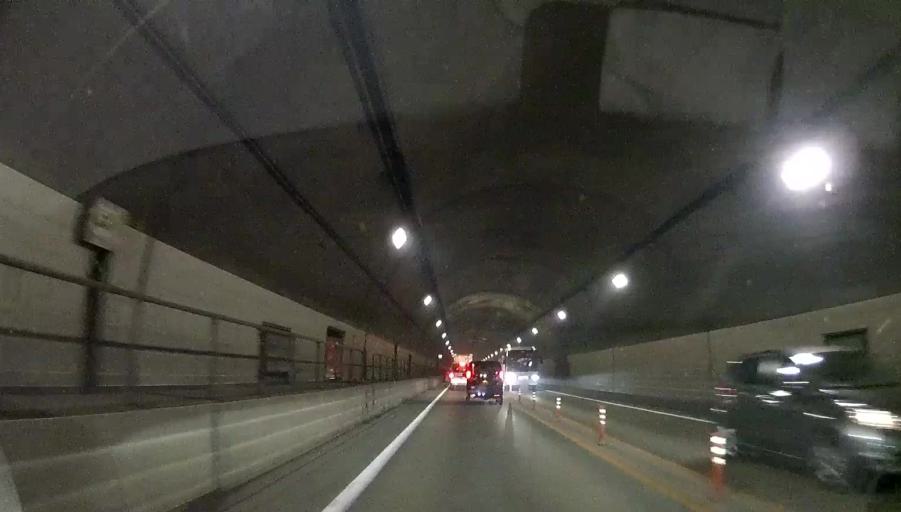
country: JP
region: Hokkaido
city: Shimo-furano
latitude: 43.0392
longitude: 142.4711
